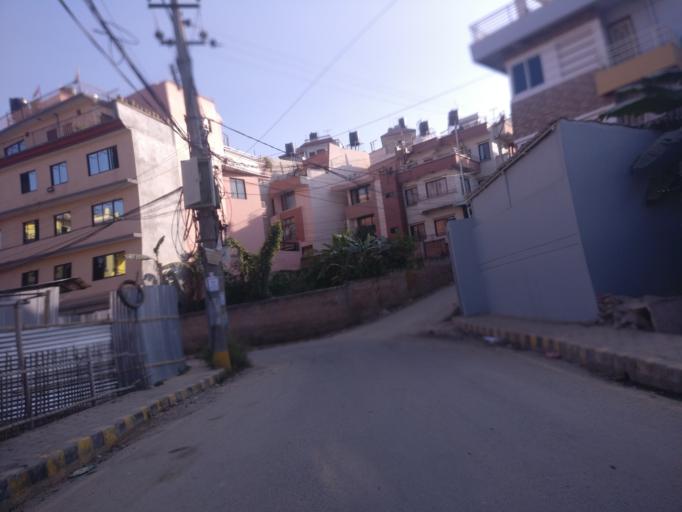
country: NP
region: Central Region
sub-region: Bagmati Zone
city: Patan
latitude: 27.6583
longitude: 85.3306
